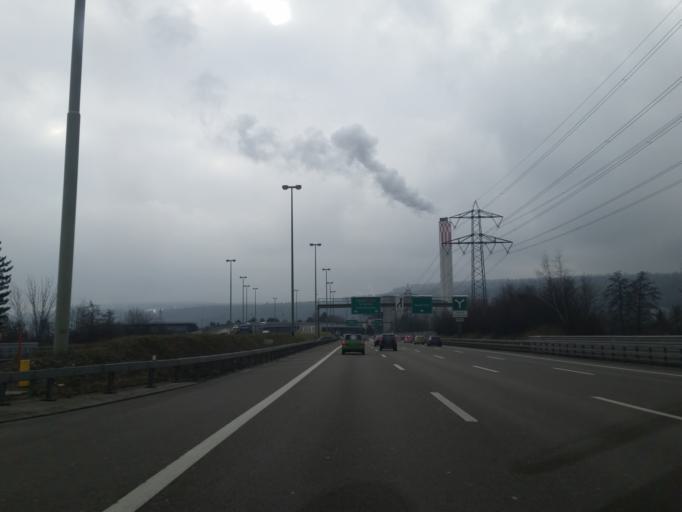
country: CH
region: Zurich
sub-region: Bezirk Zuerich
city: Zuerich (Kreis 12) / Auzelg
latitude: 47.4173
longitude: 8.5742
